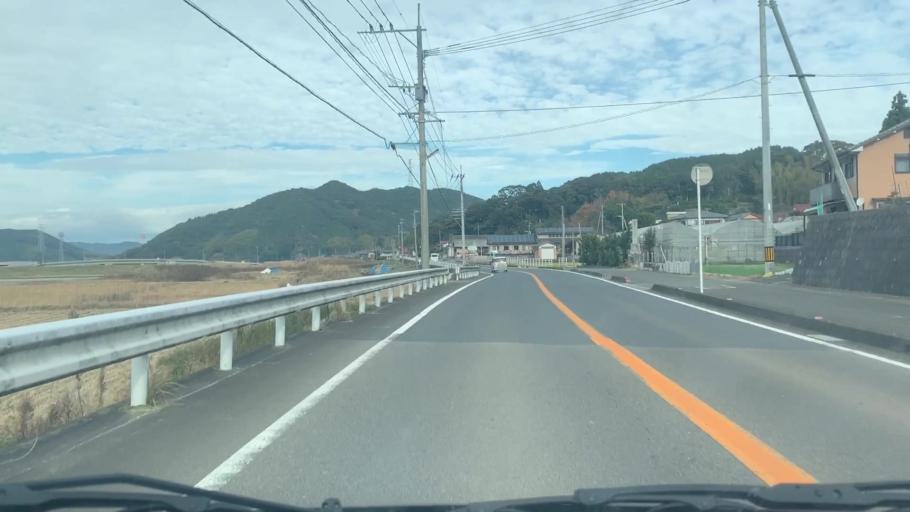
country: JP
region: Saga Prefecture
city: Karatsu
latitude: 33.3695
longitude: 130.0039
